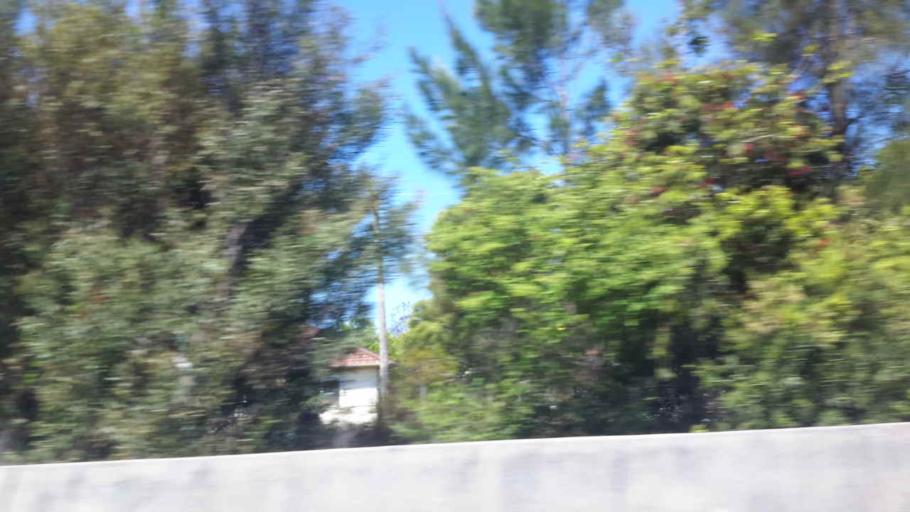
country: AU
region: New South Wales
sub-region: Wollongong
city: Bulli
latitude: -34.3458
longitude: 150.9120
